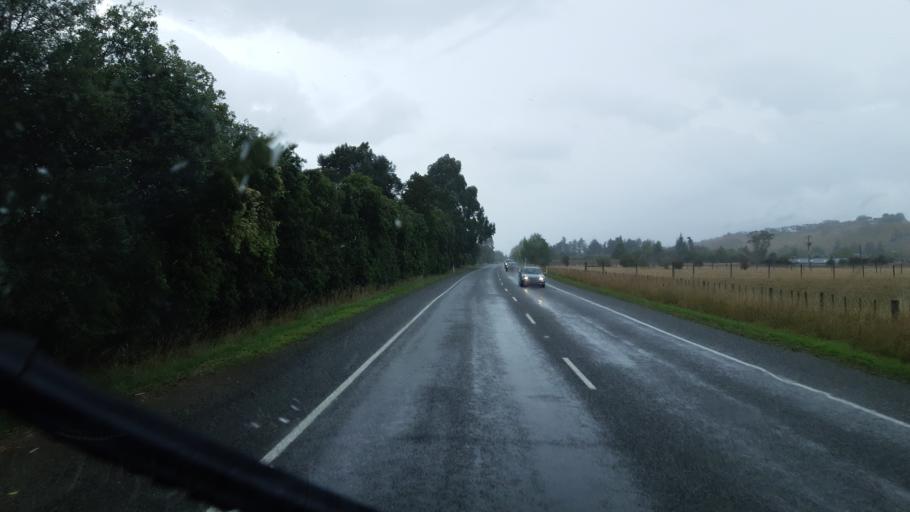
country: NZ
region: Tasman
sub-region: Tasman District
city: Brightwater
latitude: -41.3811
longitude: 173.0877
